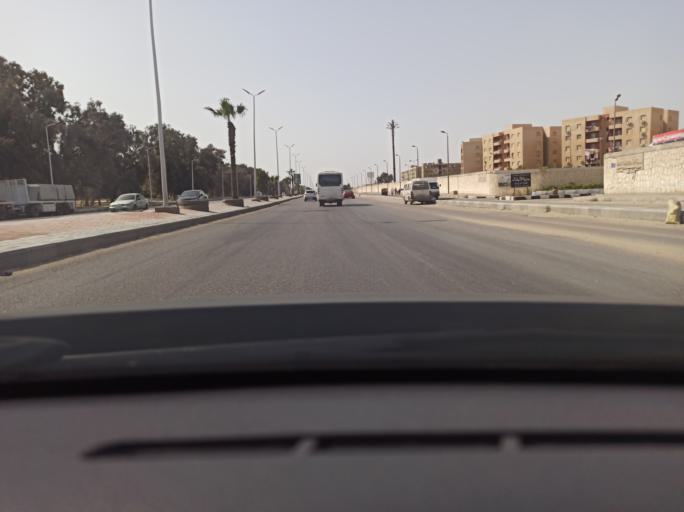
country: EG
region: Muhafazat al Qahirah
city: Halwan
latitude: 29.8289
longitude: 31.3547
